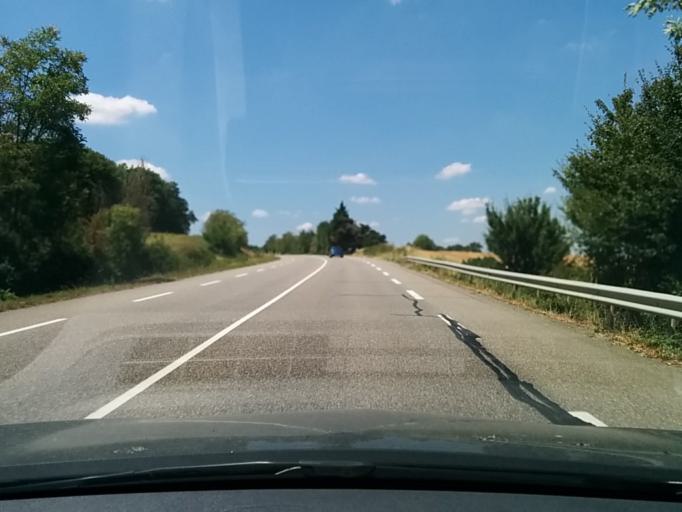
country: FR
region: Midi-Pyrenees
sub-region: Departement du Gers
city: Jegun
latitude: 43.7201
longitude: 0.4152
